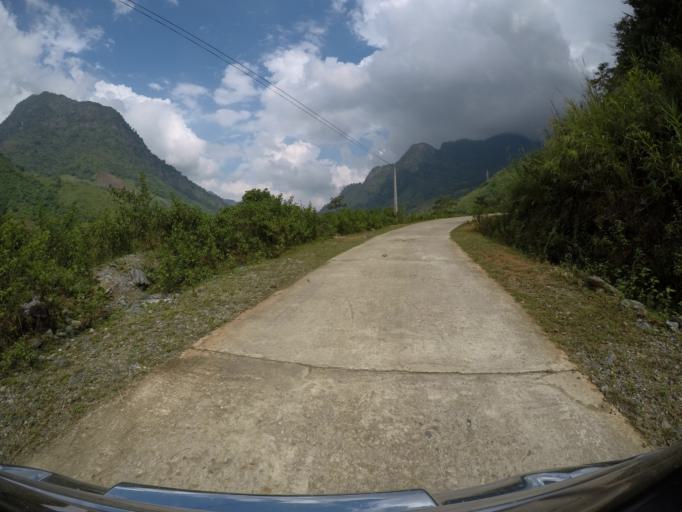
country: VN
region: Yen Bai
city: Son Thinh
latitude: 21.6803
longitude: 104.5472
